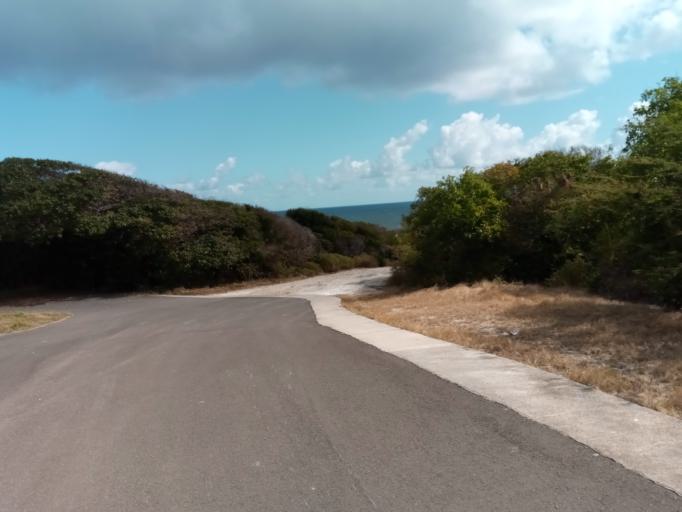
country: GP
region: Guadeloupe
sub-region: Guadeloupe
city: Saint-Francois
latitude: 16.2773
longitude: -61.2482
